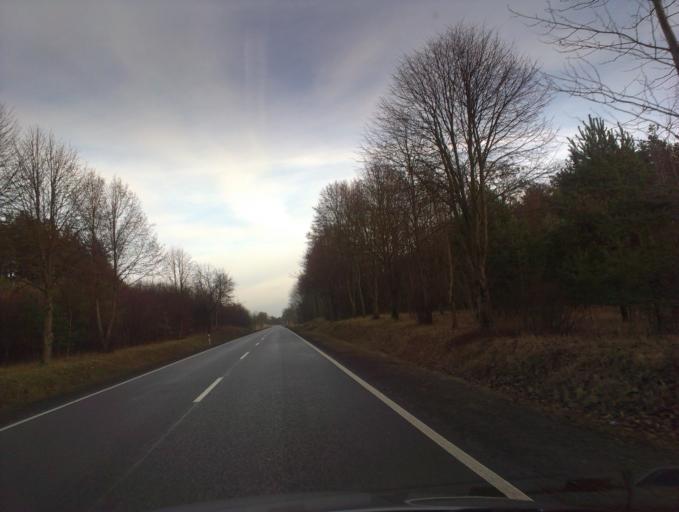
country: PL
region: West Pomeranian Voivodeship
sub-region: Powiat szczecinecki
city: Szczecinek
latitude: 53.7352
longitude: 16.7814
